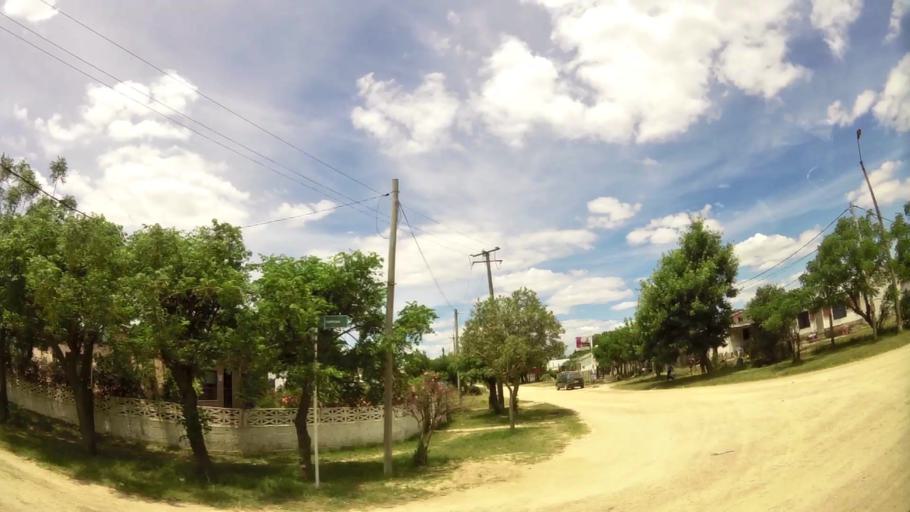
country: UY
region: San Jose
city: Delta del Tigre
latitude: -34.7725
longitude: -56.3752
